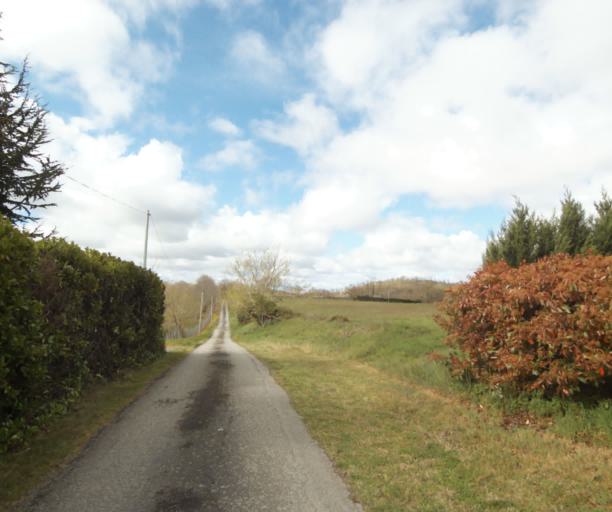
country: FR
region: Midi-Pyrenees
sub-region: Departement de l'Ariege
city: Saverdun
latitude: 43.2137
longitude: 1.5651
